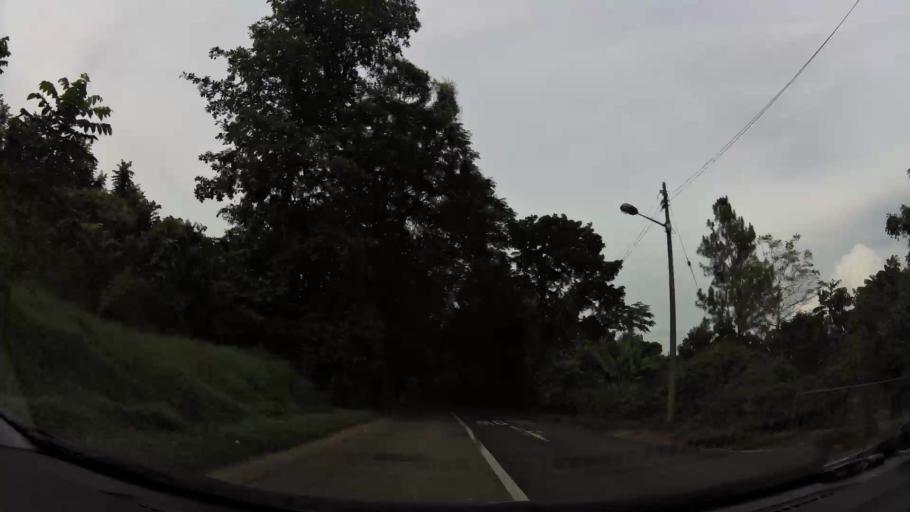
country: MY
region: Johor
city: Johor Bahru
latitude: 1.4330
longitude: 103.7078
